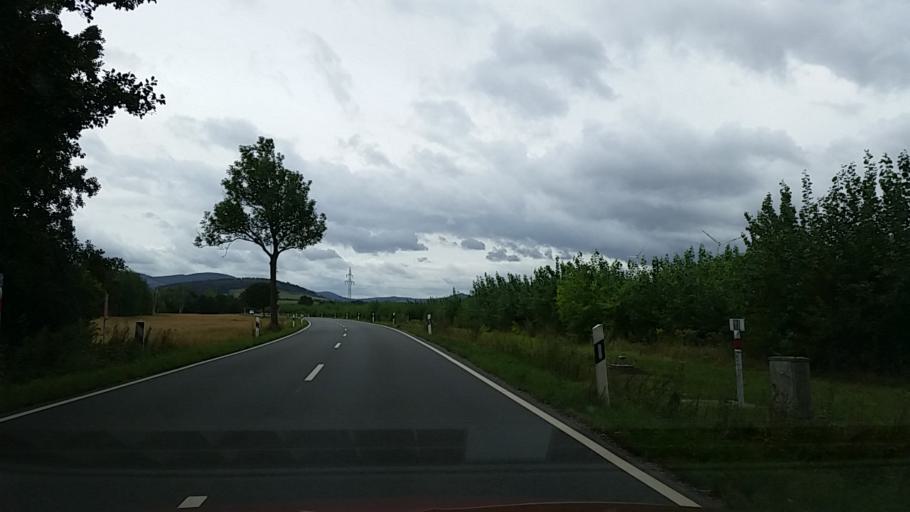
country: DE
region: Lower Saxony
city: Vienenburg
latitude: 51.9444
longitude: 10.5131
